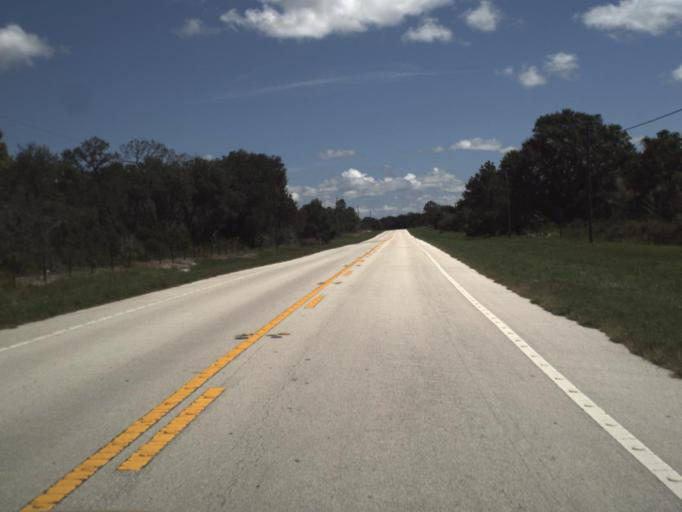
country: US
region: Florida
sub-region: Polk County
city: Frostproof
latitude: 27.6947
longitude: -81.5424
